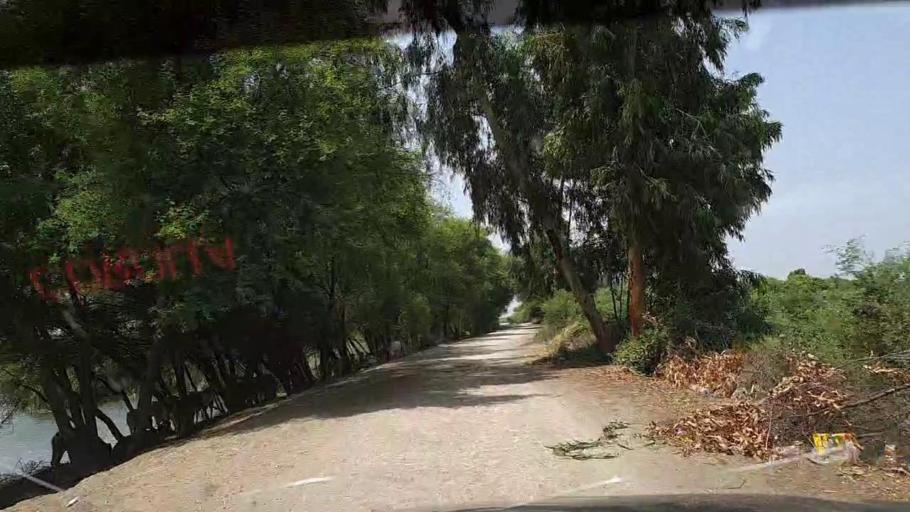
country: PK
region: Sindh
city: Ghotki
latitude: 28.0964
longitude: 69.3125
